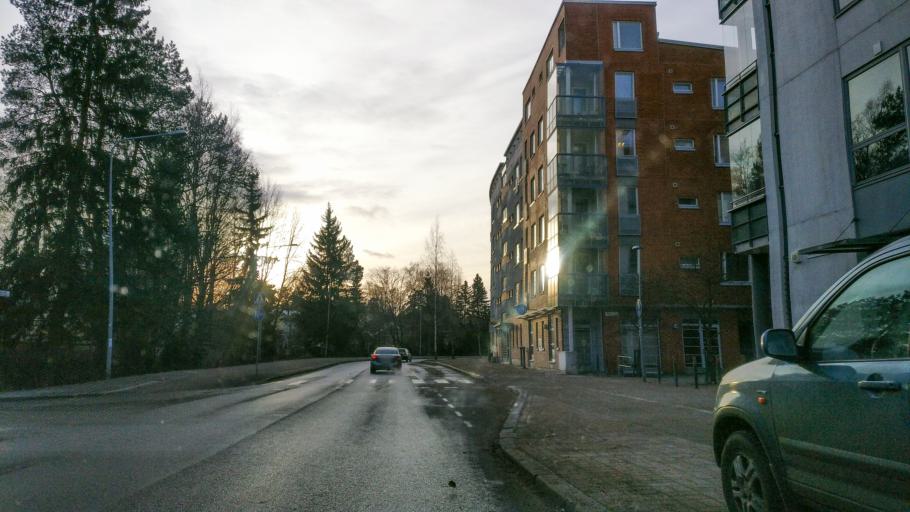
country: FI
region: Uusimaa
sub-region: Helsinki
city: Vantaa
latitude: 60.2045
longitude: 25.0764
